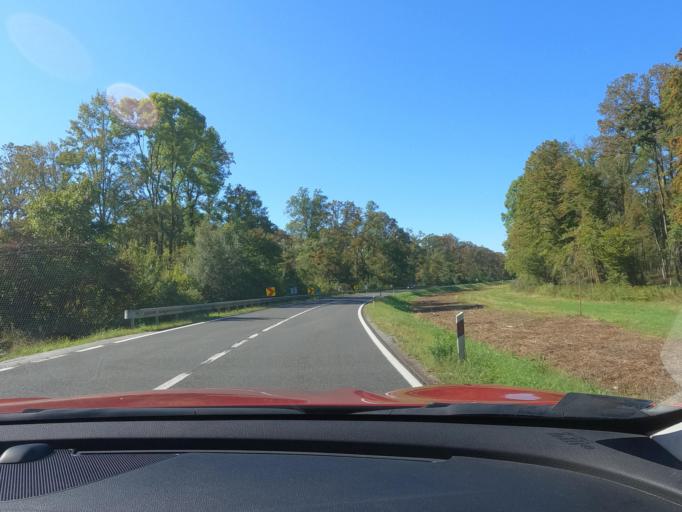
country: HR
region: Sisacko-Moslavacka
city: Budasevo
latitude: 45.4948
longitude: 16.5087
